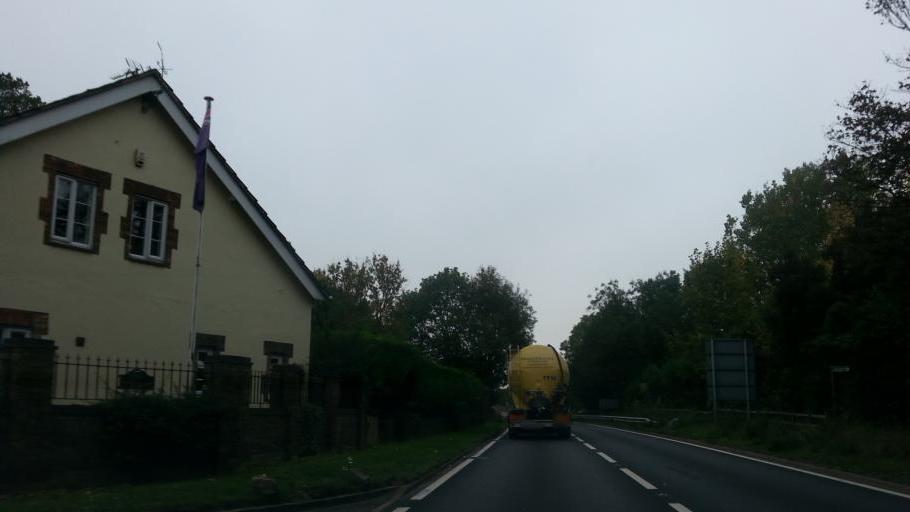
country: GB
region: England
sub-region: Northamptonshire
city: Thrapston
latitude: 52.4205
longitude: -0.4966
